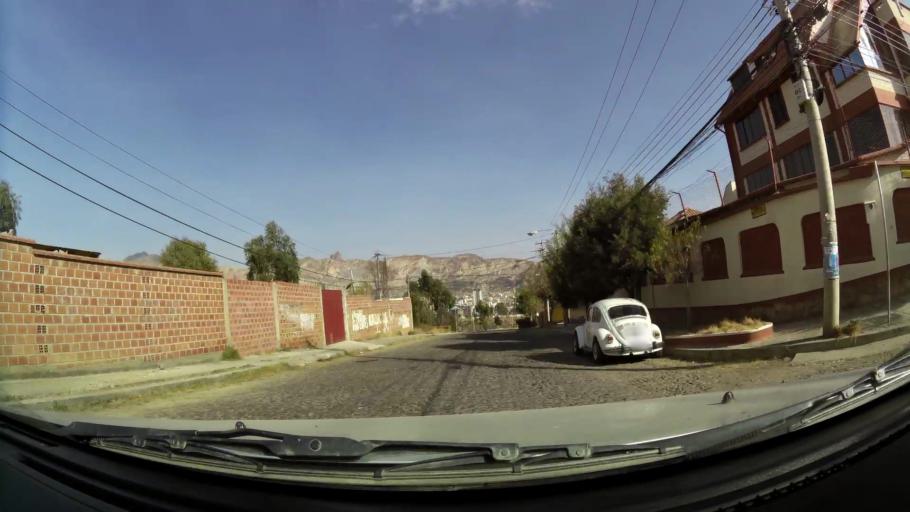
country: BO
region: La Paz
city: La Paz
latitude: -16.5274
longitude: -68.0795
